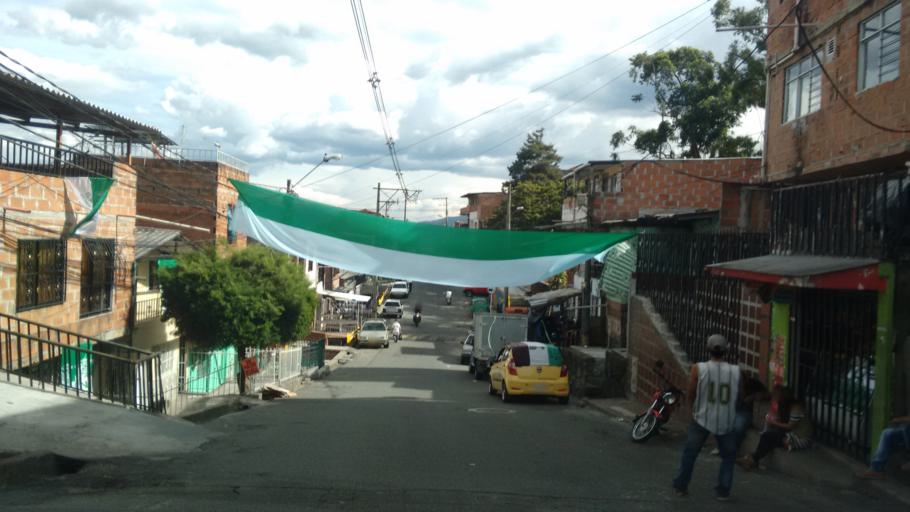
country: CO
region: Antioquia
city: Medellin
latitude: 6.2936
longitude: -75.5803
